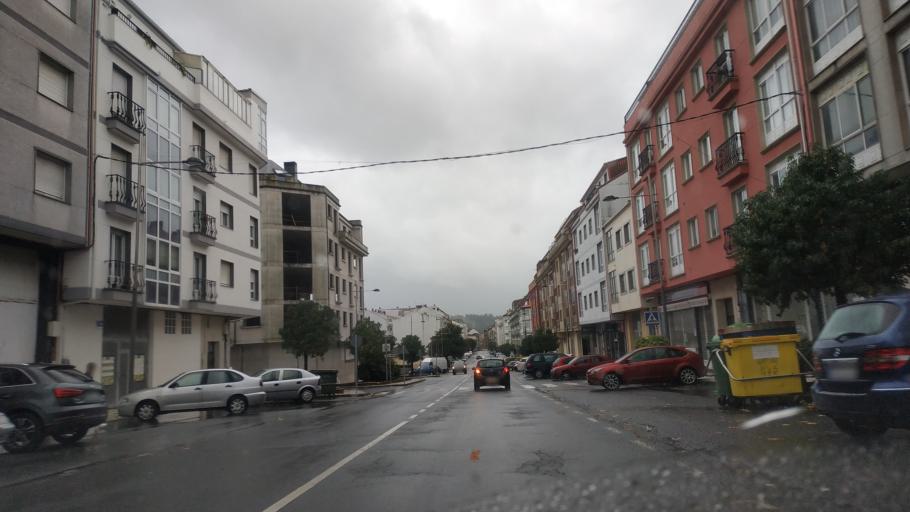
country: ES
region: Galicia
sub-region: Provincia da Coruna
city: Negreira
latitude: 42.9157
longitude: -8.7352
